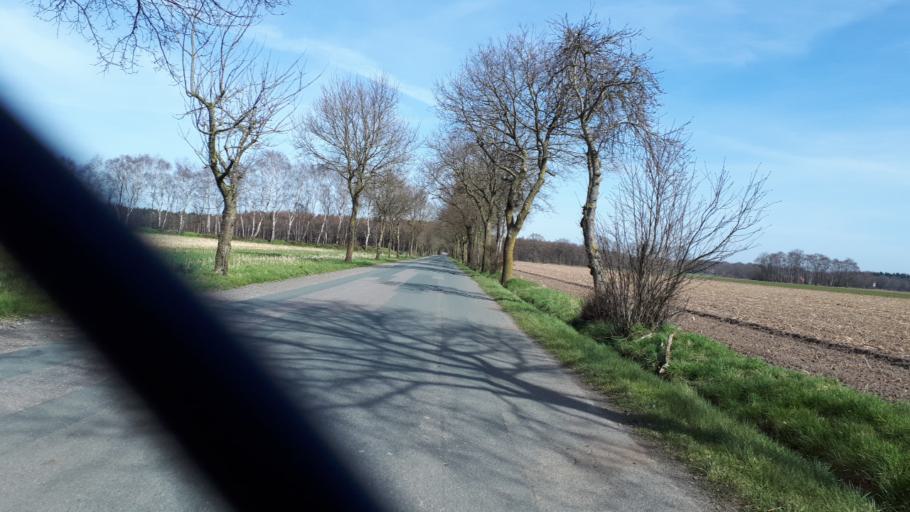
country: DE
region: Lower Saxony
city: Cloppenburg
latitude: 52.8800
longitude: 8.0009
